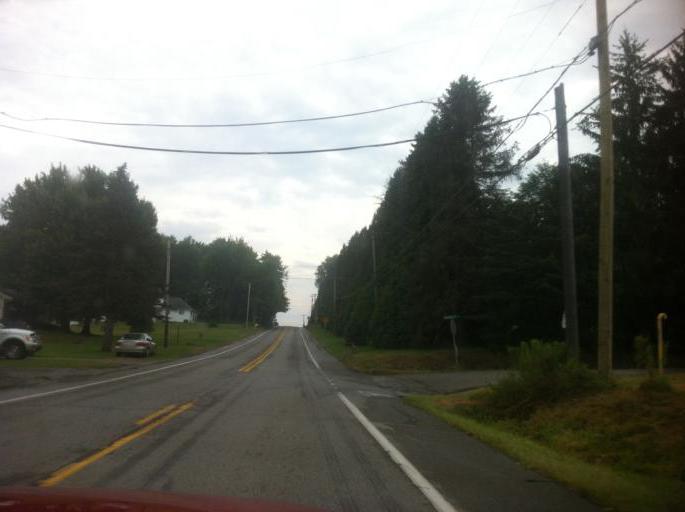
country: US
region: Pennsylvania
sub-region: Mercer County
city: Grove City
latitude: 41.1912
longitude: -80.0819
